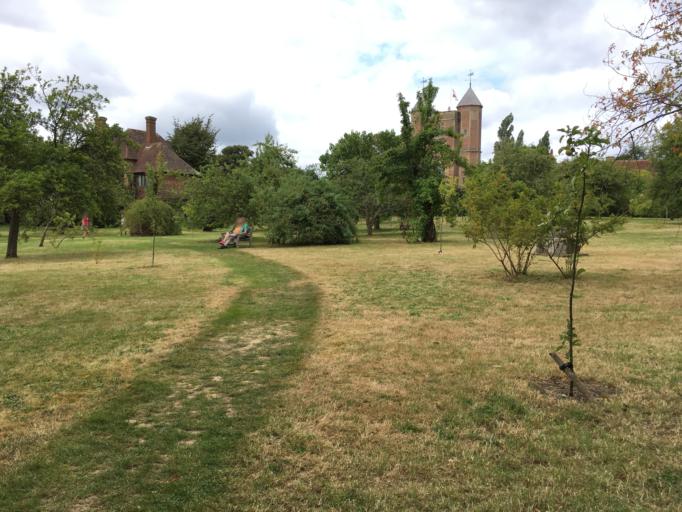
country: GB
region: England
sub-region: Kent
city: Cranbrook
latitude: 51.1156
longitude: 0.5833
